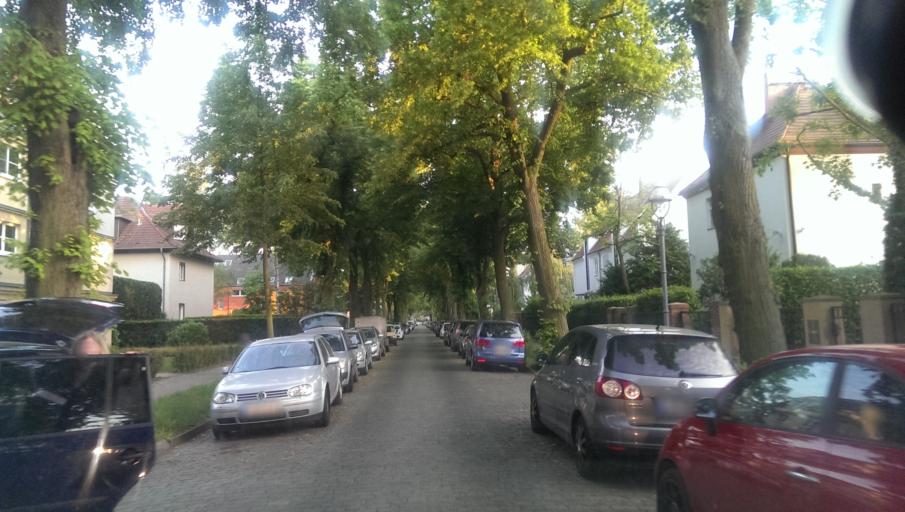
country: DE
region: Berlin
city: Lichterfelde
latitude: 52.4278
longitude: 13.2925
